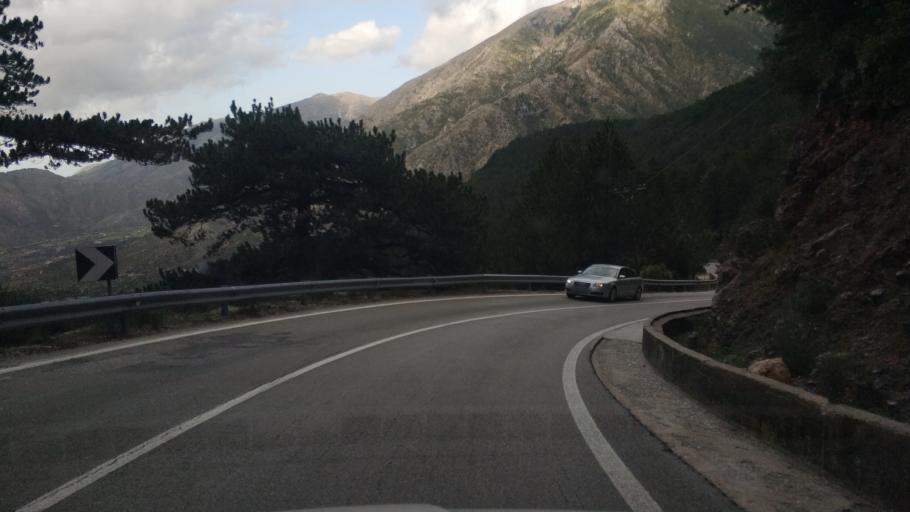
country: AL
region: Vlore
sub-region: Rrethi i Vlores
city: Brataj
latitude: 40.2200
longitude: 19.5786
